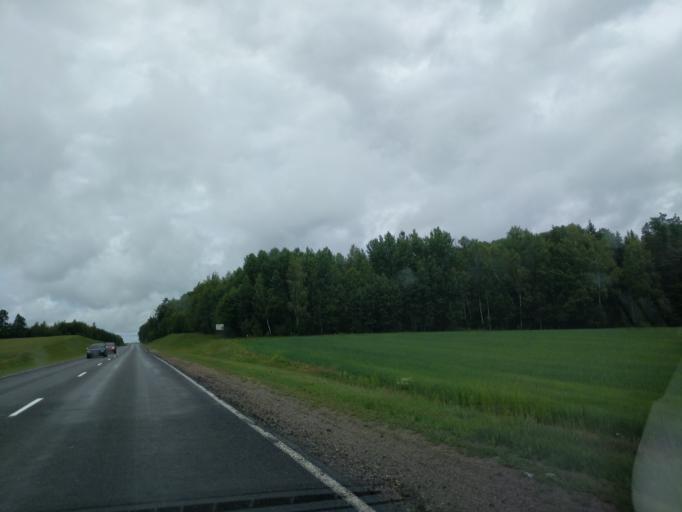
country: BY
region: Minsk
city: Il'ya
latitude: 54.3104
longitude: 27.4722
